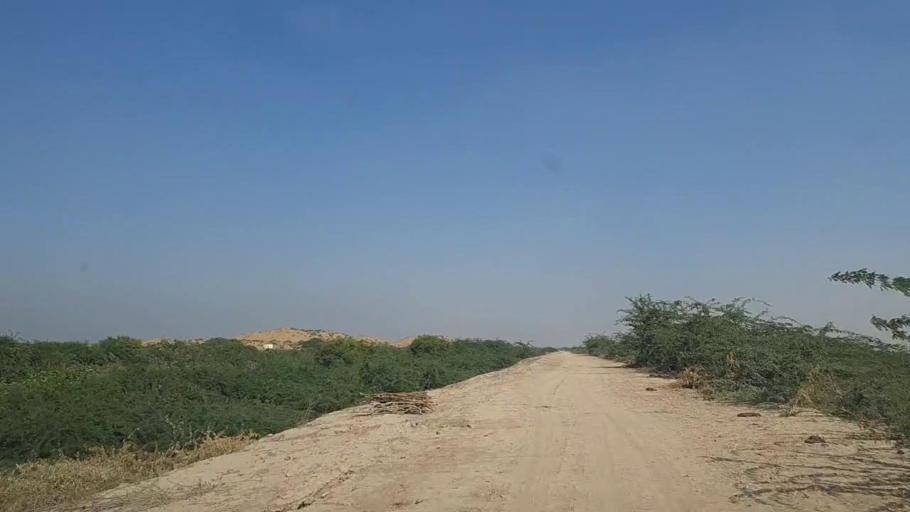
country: PK
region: Sindh
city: Daro Mehar
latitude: 24.8637
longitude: 68.0415
